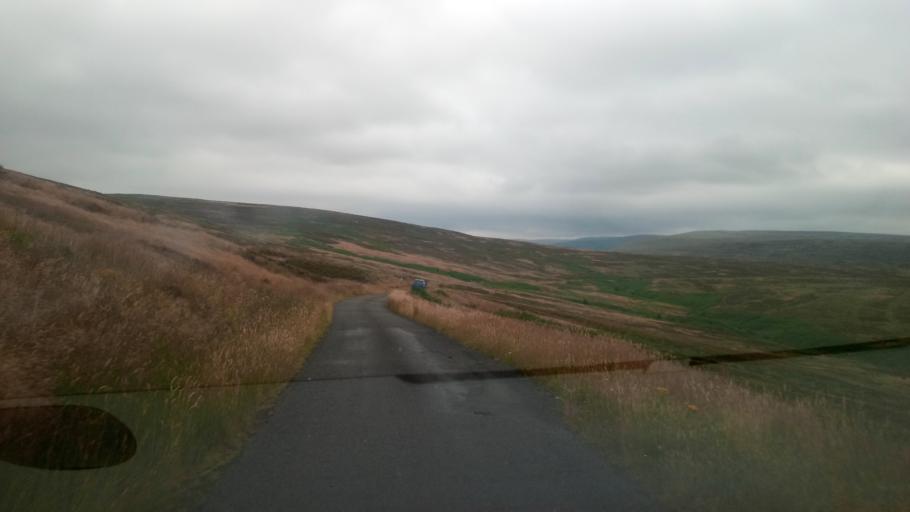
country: GB
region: Scotland
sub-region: Dumfries and Galloway
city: Langholm
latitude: 55.1642
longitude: -2.9623
